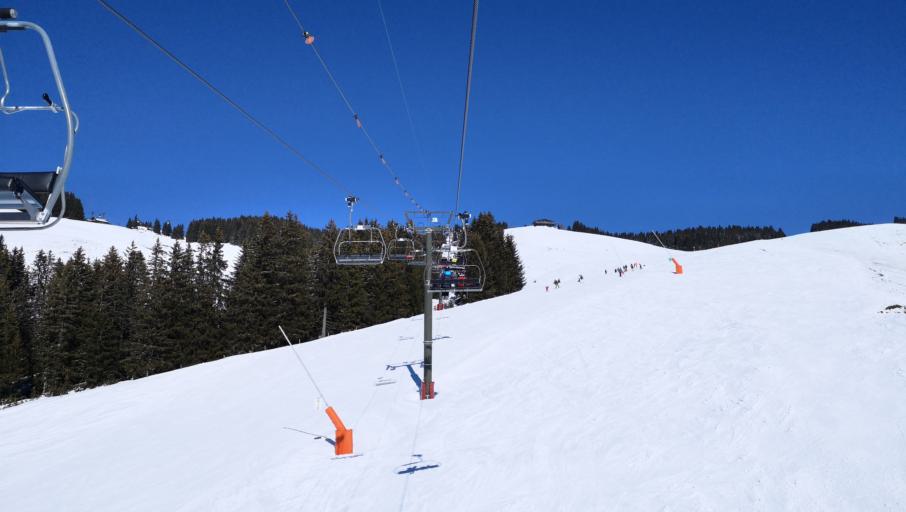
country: FR
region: Rhone-Alpes
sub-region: Departement de la Haute-Savoie
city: Megeve
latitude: 45.8505
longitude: 6.6548
